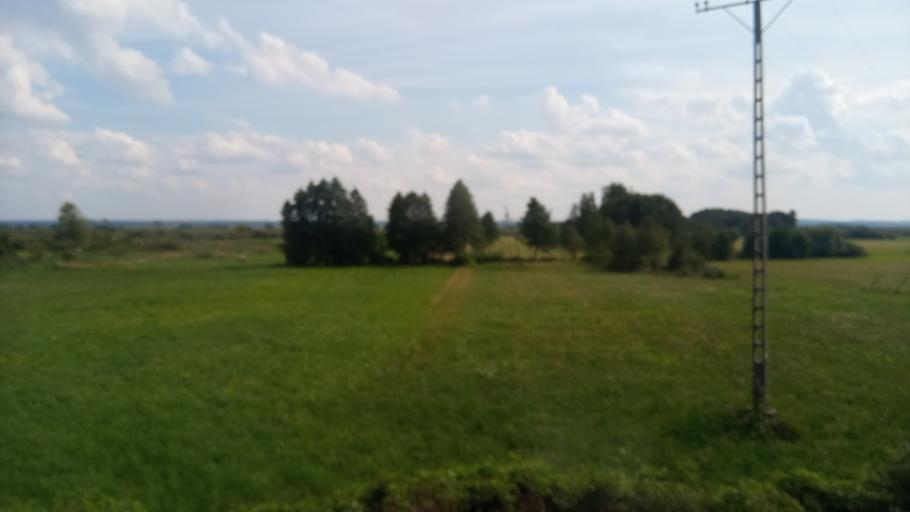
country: PL
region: Greater Poland Voivodeship
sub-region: Powiat pilski
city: Miasteczko Krajenskie
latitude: 53.0927
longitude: 17.0113
